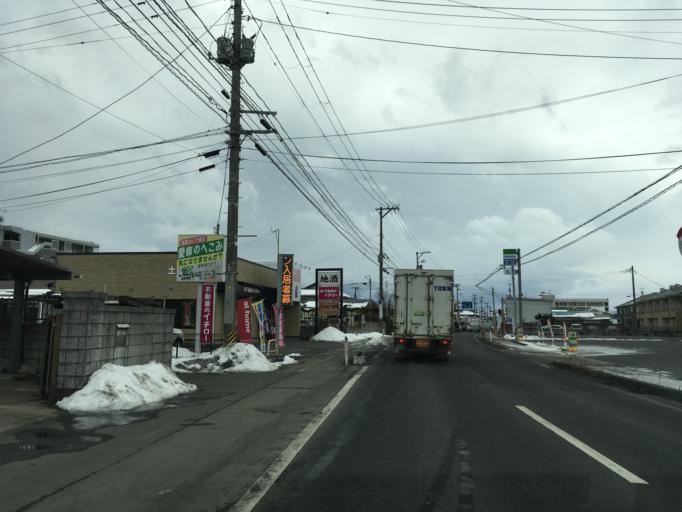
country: JP
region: Miyagi
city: Furukawa
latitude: 38.5836
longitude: 140.9665
